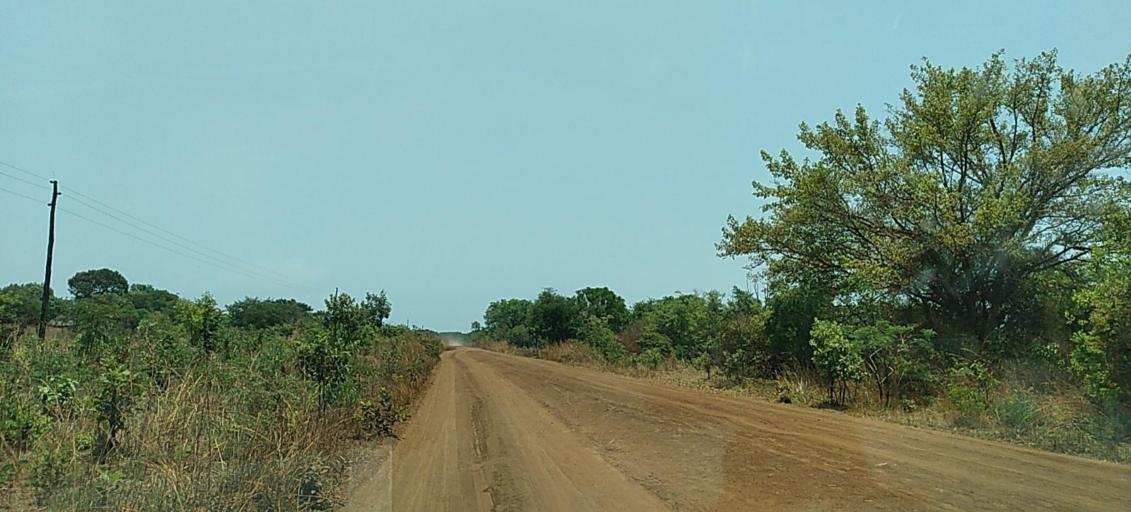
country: ZM
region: Copperbelt
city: Mpongwe
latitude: -13.6967
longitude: 27.8650
